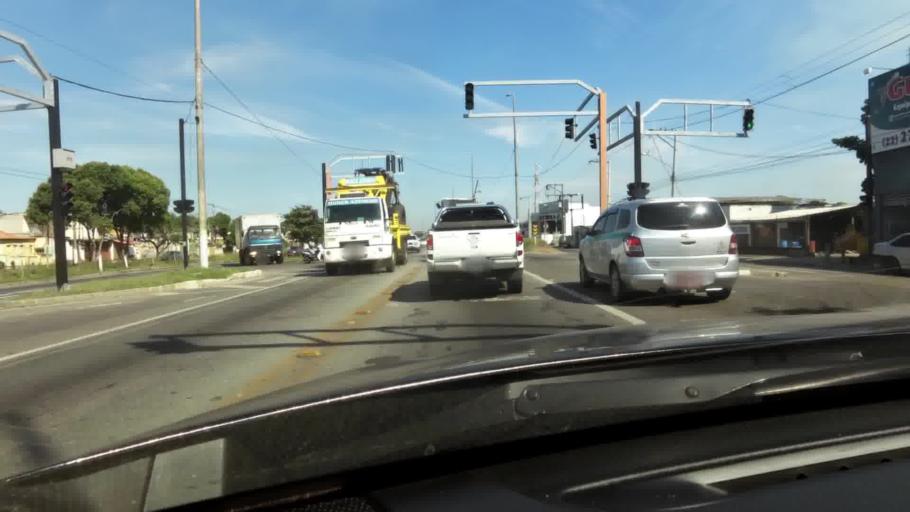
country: BR
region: Rio de Janeiro
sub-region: Campos Dos Goytacazes
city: Campos
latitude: -21.7245
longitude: -41.3197
